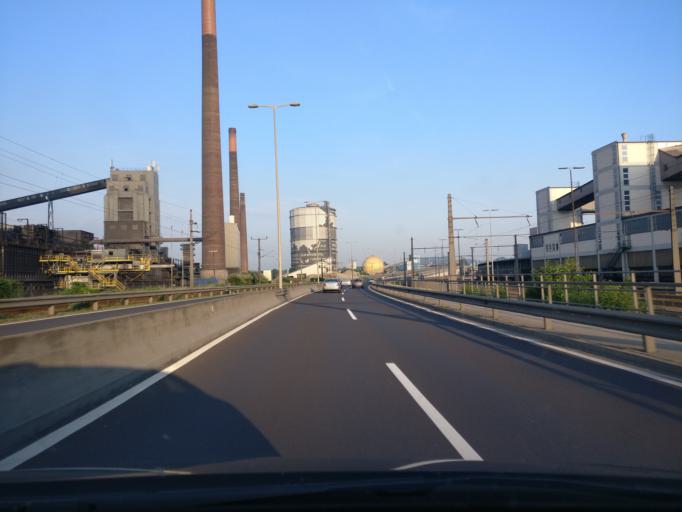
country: AT
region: Upper Austria
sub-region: Politischer Bezirk Urfahr-Umgebung
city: Steyregg
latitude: 48.2851
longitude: 14.3327
